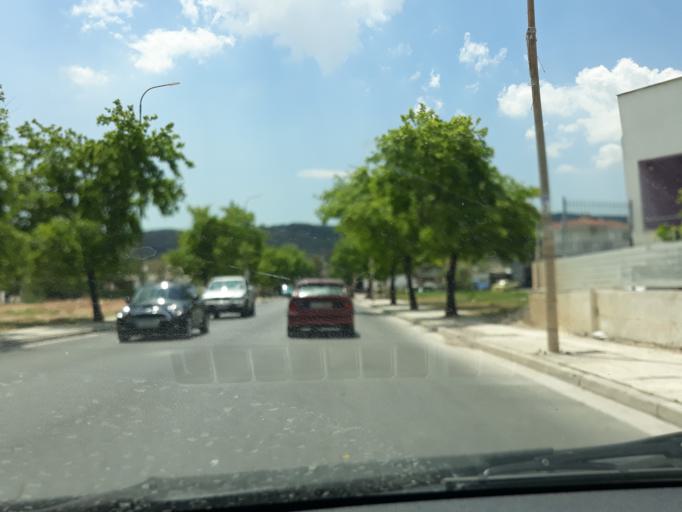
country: GR
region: Attica
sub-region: Nomarchia Dytikis Attikis
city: Ano Liosia
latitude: 38.0765
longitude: 23.7081
